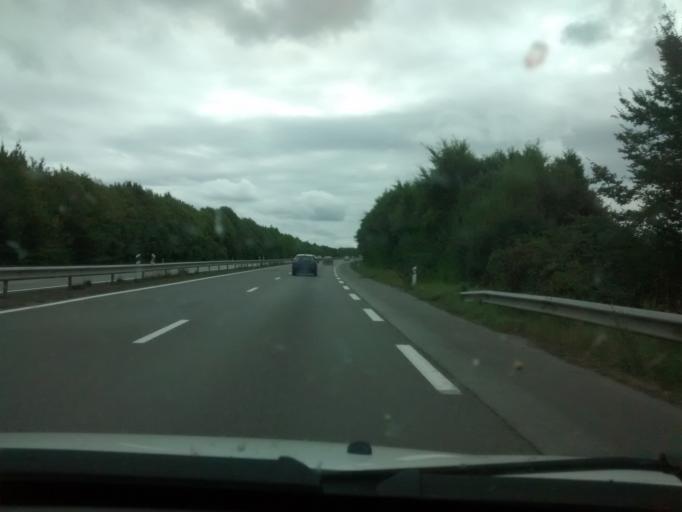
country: FR
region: Brittany
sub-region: Departement d'Ille-et-Vilaine
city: Saint-Domineuc
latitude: 48.3516
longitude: -1.8645
